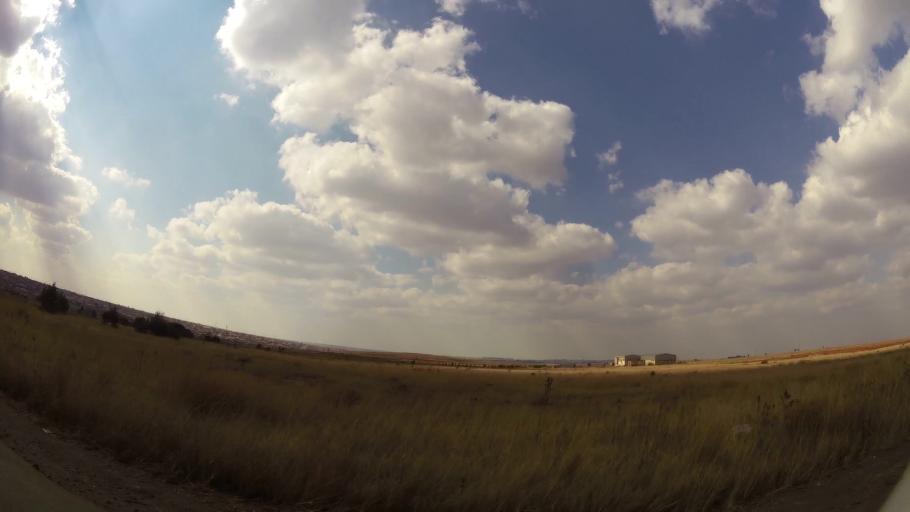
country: ZA
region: Mpumalanga
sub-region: Nkangala District Municipality
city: Delmas
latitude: -26.1128
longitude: 28.6794
